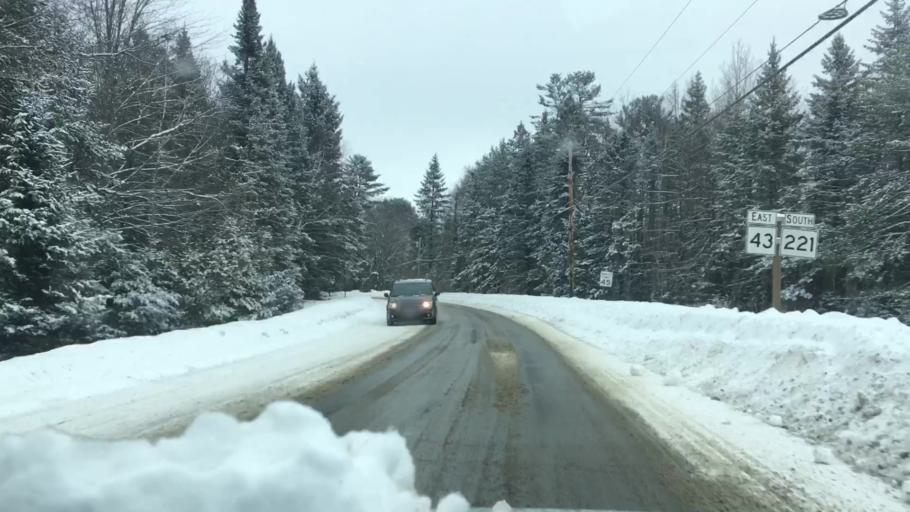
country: US
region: Maine
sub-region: Penobscot County
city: Hudson
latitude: 45.0213
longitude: -68.9141
